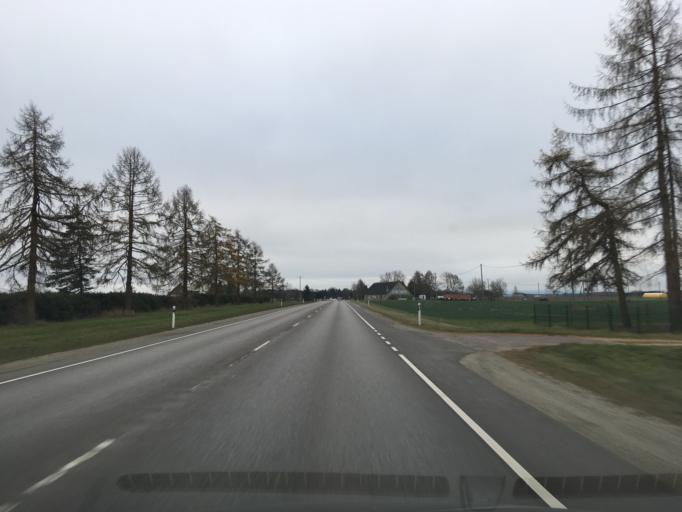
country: EE
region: Laeaene-Virumaa
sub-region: Rakvere linn
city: Rakvere
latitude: 59.4053
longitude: 26.3651
